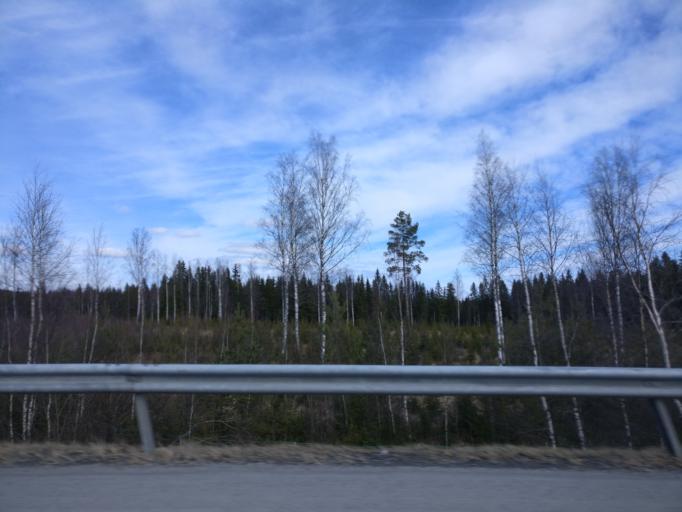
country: FI
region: Haeme
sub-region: Haemeenlinna
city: Kalvola
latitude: 61.1259
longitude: 24.1158
